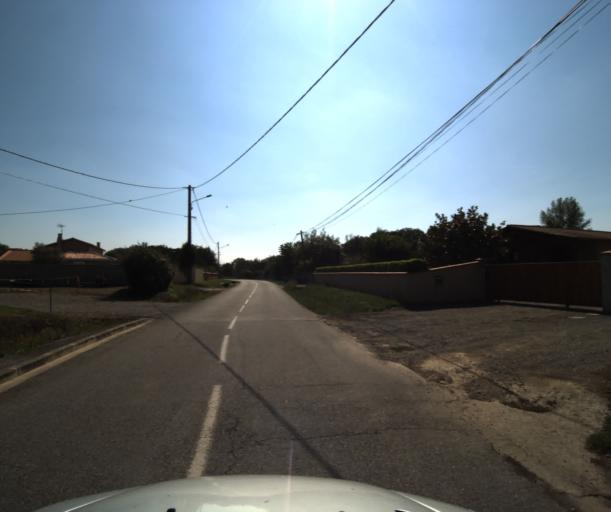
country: FR
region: Midi-Pyrenees
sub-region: Departement de la Haute-Garonne
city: Lacasse
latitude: 43.3908
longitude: 1.2520
